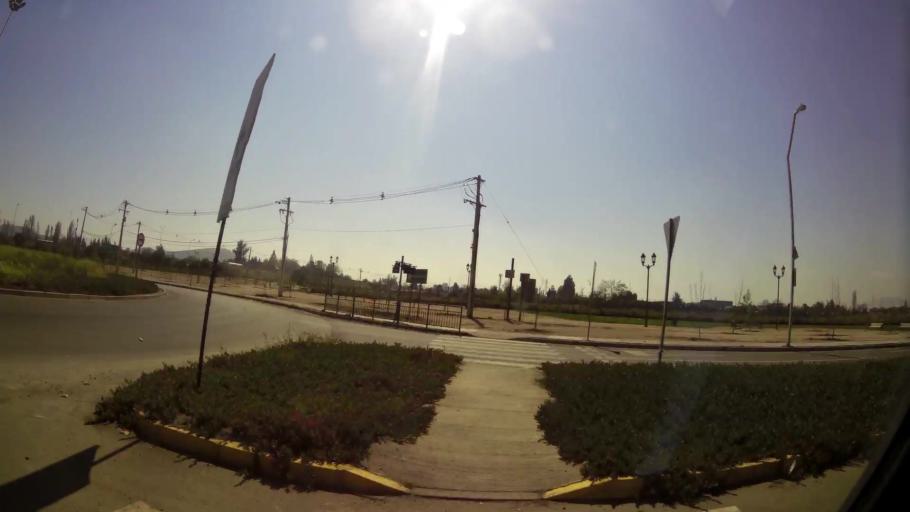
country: CL
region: Santiago Metropolitan
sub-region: Provincia de Talagante
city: Penaflor
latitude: -33.5605
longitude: -70.8274
